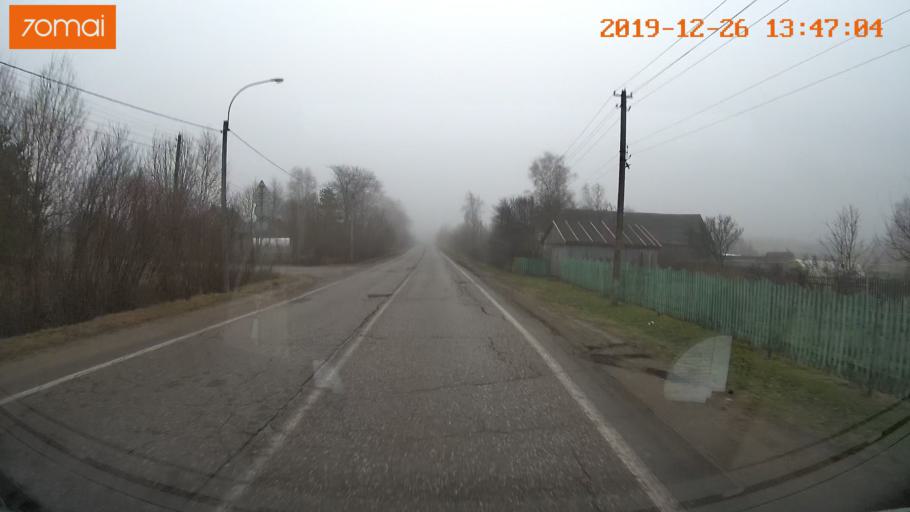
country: RU
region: Vologda
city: Sheksna
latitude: 58.6874
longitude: 38.5308
